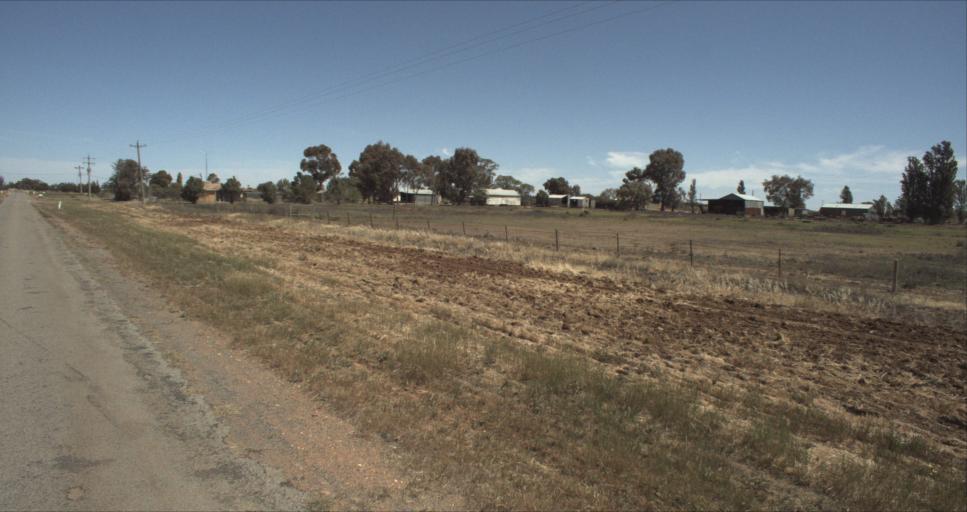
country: AU
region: New South Wales
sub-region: Leeton
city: Leeton
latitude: -34.5095
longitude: 146.3447
